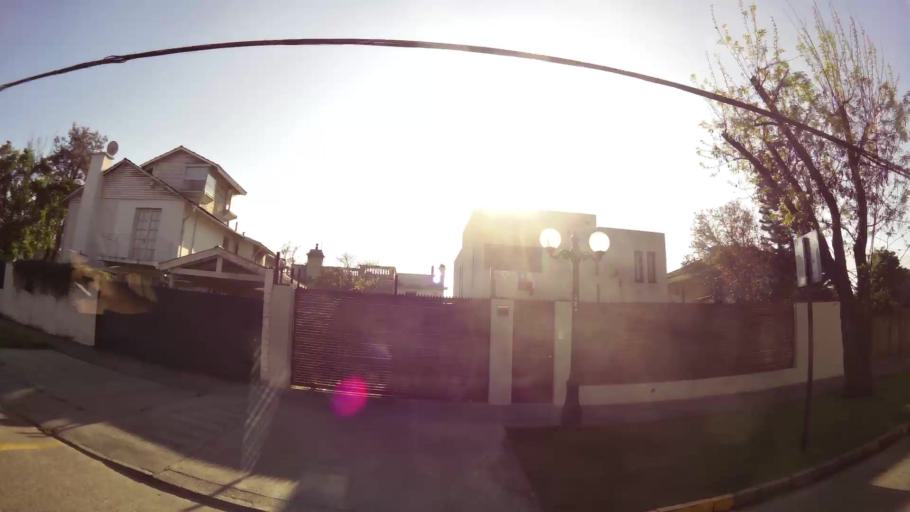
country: CL
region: Santiago Metropolitan
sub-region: Provincia de Santiago
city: Villa Presidente Frei, Nunoa, Santiago, Chile
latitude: -33.4393
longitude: -70.5956
